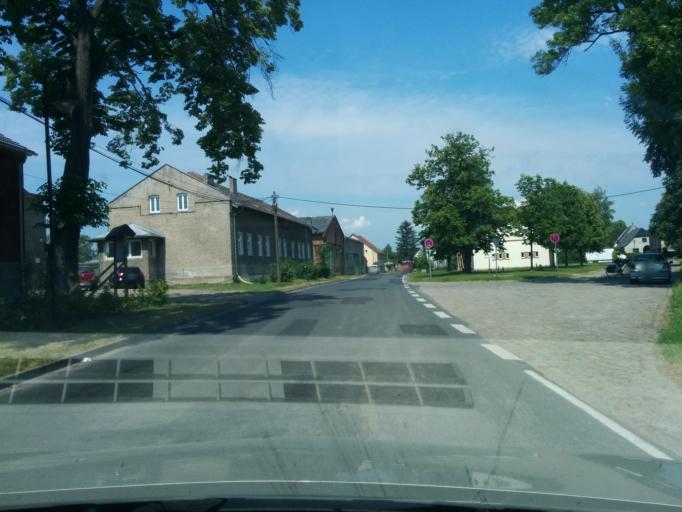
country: DE
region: Brandenburg
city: Ahrensfelde
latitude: 52.6249
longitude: 13.5751
